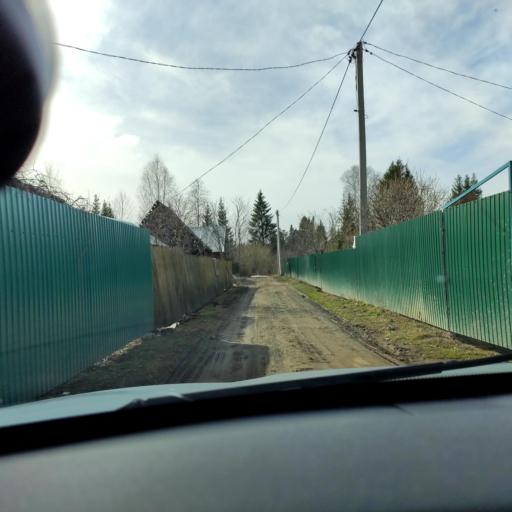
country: RU
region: Perm
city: Overyata
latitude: 58.0586
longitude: 55.9817
